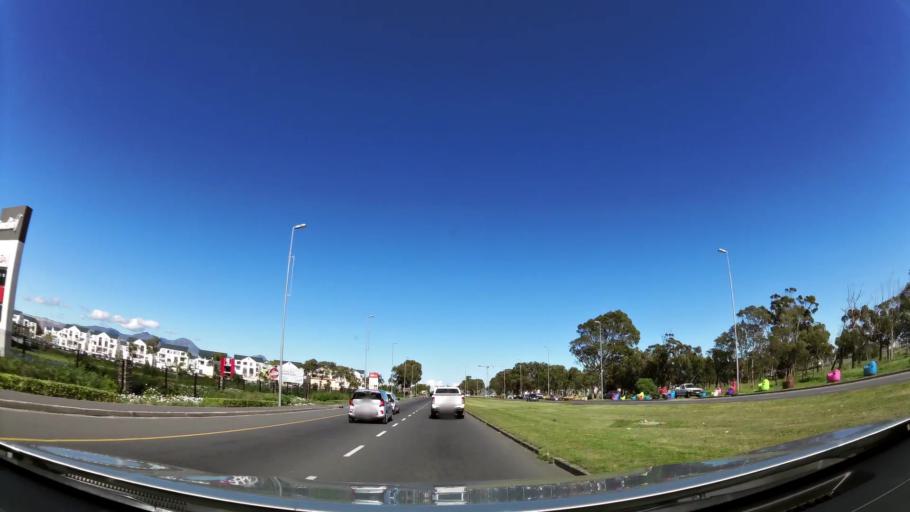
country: ZA
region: Western Cape
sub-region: Cape Winelands District Municipality
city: Stellenbosch
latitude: -34.0879
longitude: 18.8198
